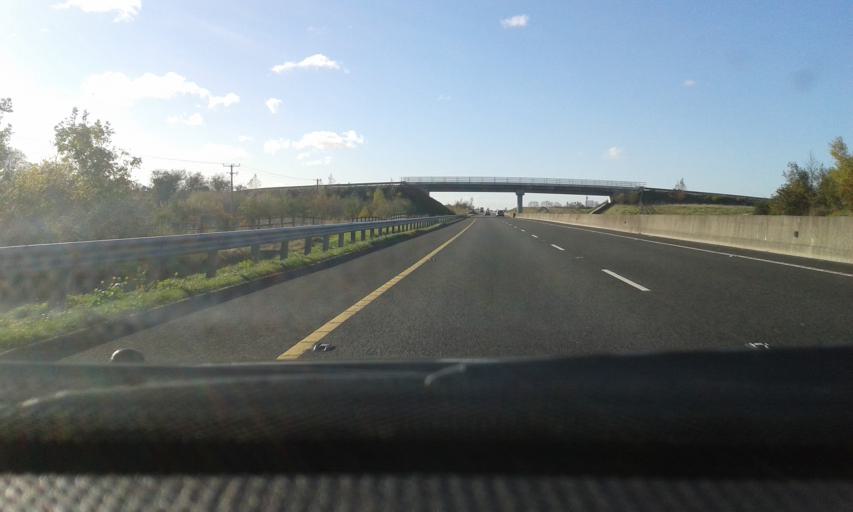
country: IE
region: Leinster
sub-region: Laois
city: Rathdowney
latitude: 52.7910
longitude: -7.5202
